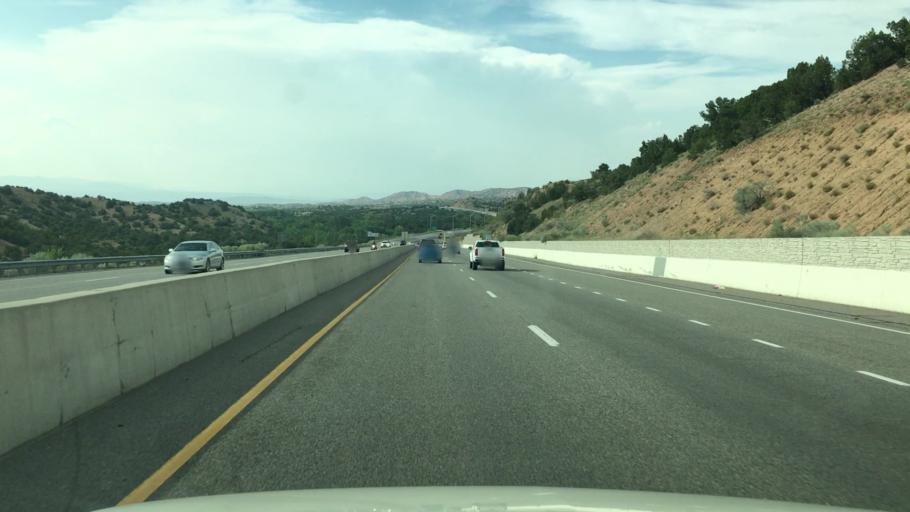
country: US
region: New Mexico
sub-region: Santa Fe County
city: Santa Fe
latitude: 35.7749
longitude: -105.9456
